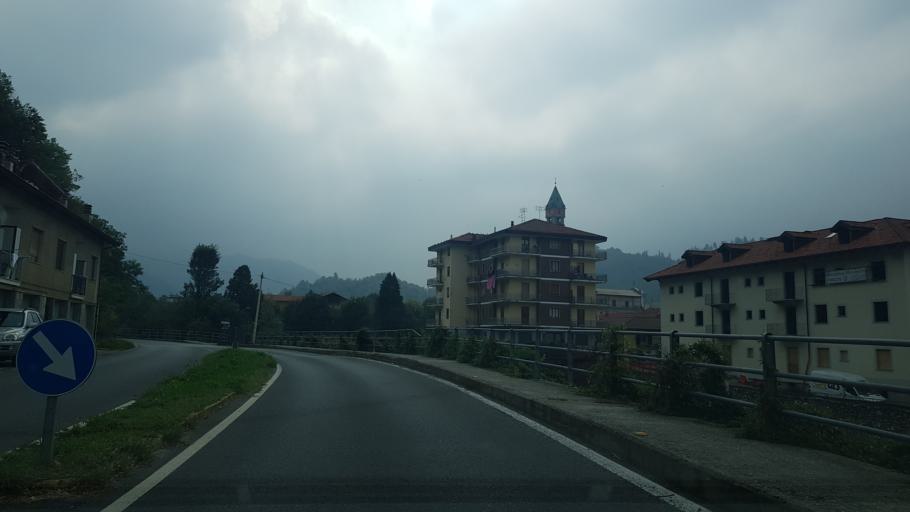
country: IT
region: Piedmont
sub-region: Provincia di Cuneo
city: Chiusa di Pesio
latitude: 44.3258
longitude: 7.6799
